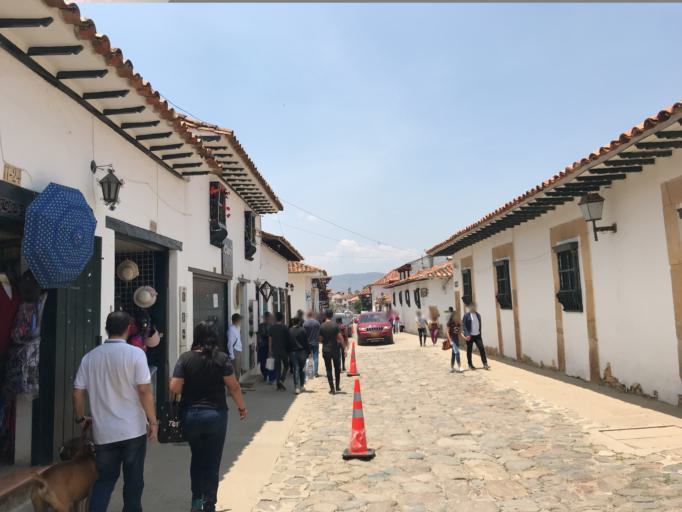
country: CO
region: Boyaca
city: Villa de Leiva
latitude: 5.6327
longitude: -73.5242
